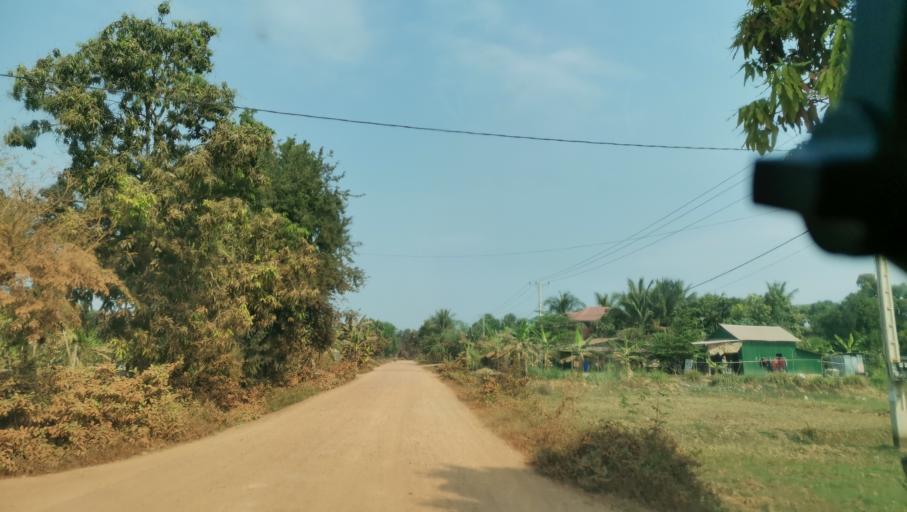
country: KH
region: Battambang
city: Battambang
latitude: 13.0611
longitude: 103.1683
